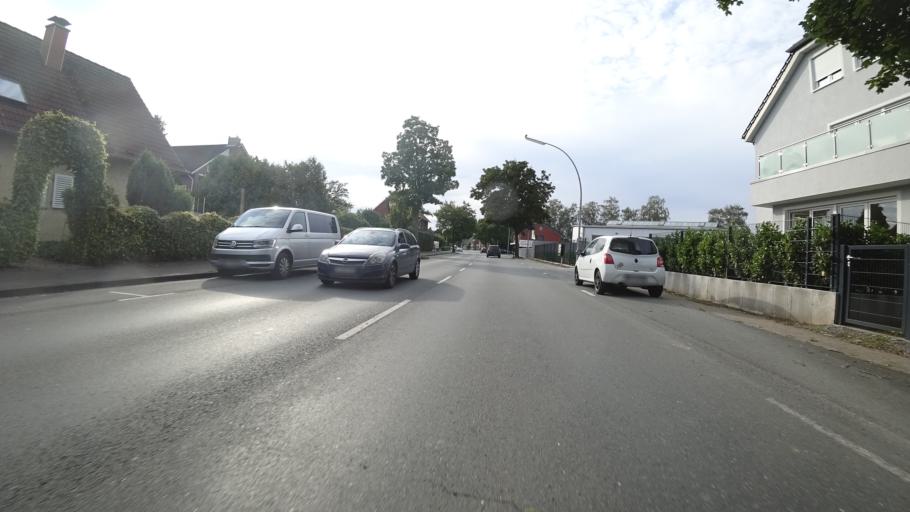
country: DE
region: North Rhine-Westphalia
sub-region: Regierungsbezirk Munster
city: Beelen
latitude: 51.9753
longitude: 8.1503
